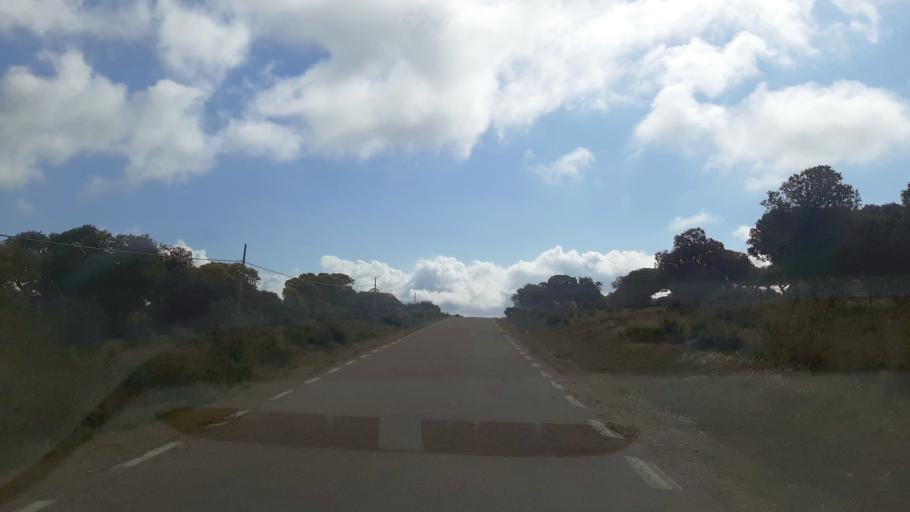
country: ES
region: Castille and Leon
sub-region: Provincia de Salamanca
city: Narros de Matalayegua
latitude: 40.7033
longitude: -5.9079
